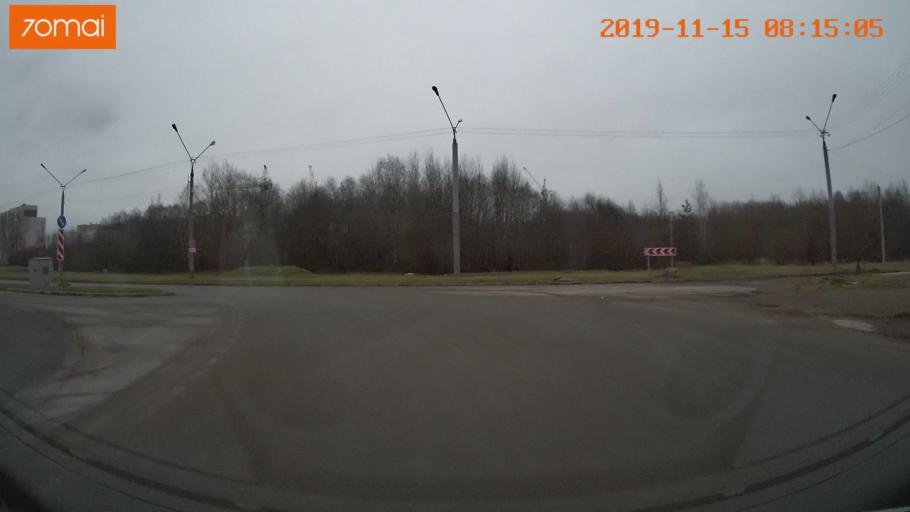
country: RU
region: Vologda
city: Cherepovets
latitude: 59.0801
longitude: 37.9236
